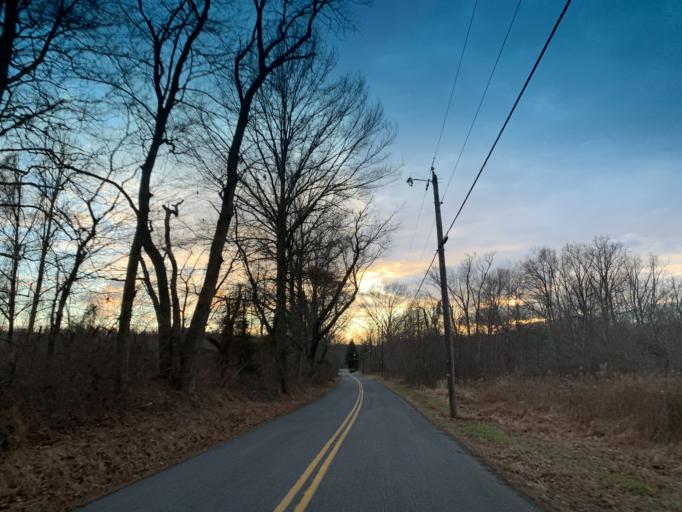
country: US
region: Maryland
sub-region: Harford County
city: Bel Air North
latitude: 39.6175
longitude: -76.3128
